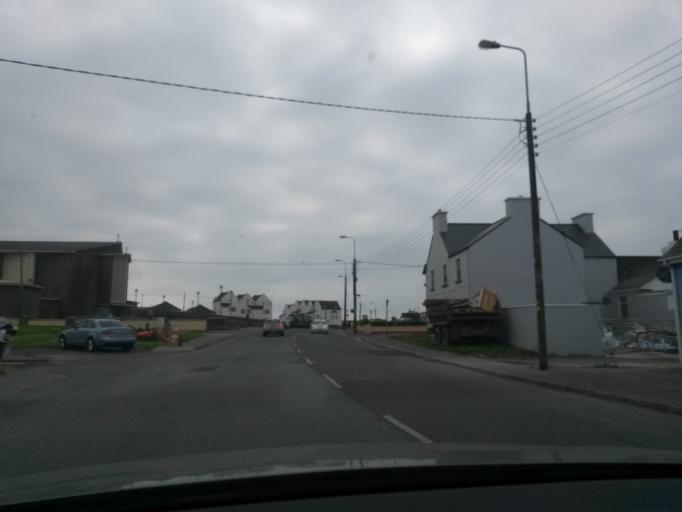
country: IE
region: Munster
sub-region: An Clar
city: Kilrush
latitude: 52.6778
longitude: -9.6445
